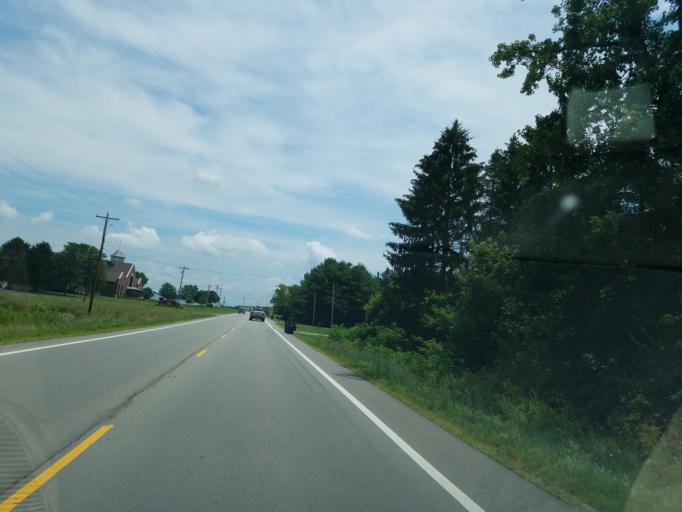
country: US
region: Ohio
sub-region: Delaware County
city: Sunbury
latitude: 40.2620
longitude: -82.8922
